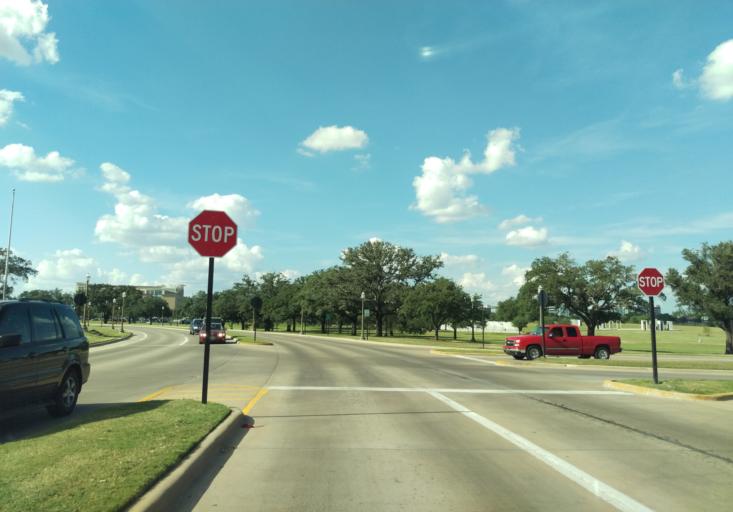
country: US
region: Texas
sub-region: Brazos County
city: College Station
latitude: 30.6195
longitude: -96.3349
